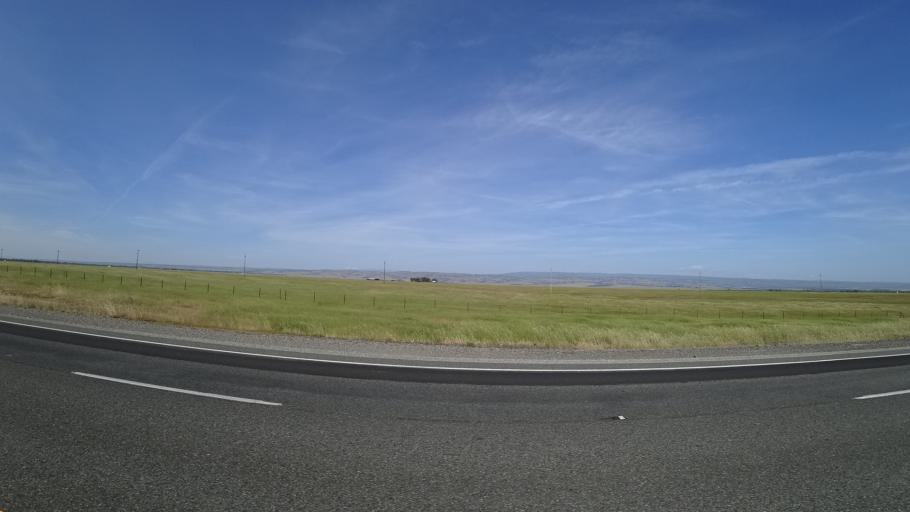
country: US
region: California
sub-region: Tehama County
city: Los Molinos
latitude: 39.9067
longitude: -122.0043
